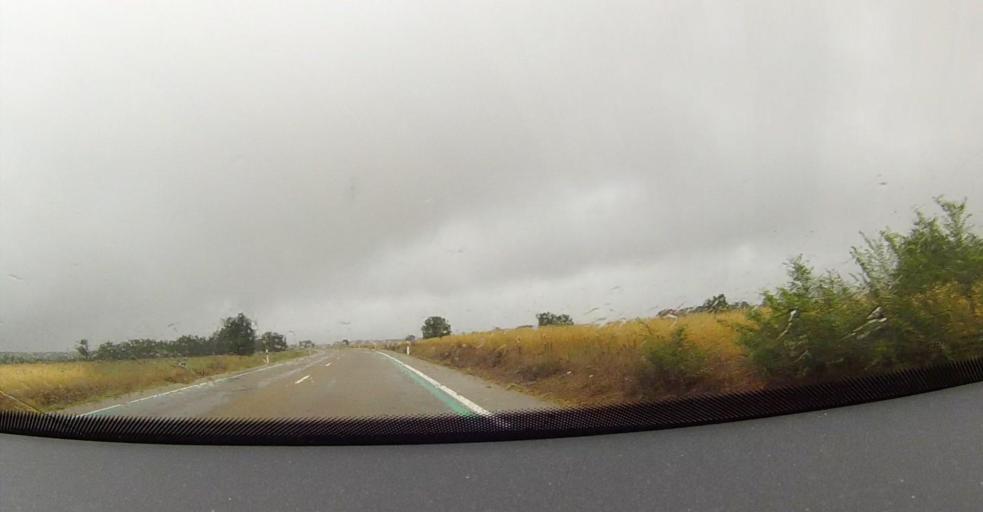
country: ES
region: Castille and Leon
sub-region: Provincia de Palencia
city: Poza de la Vega
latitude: 42.6099
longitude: -4.7654
